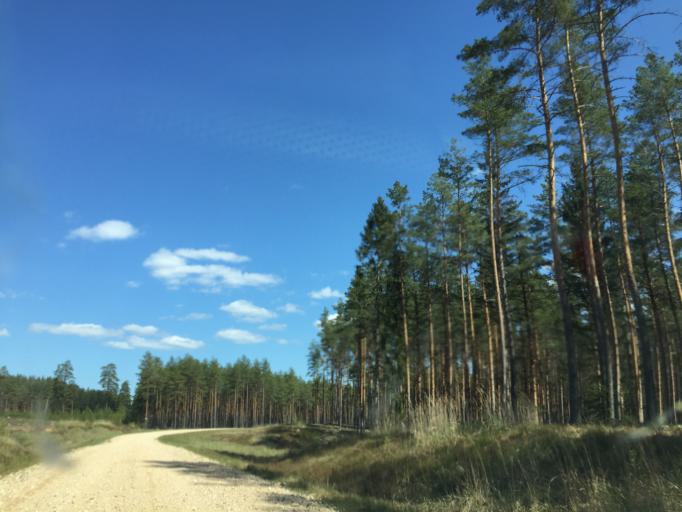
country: LV
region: Vecumnieki
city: Vecumnieki
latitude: 56.6584
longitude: 24.4845
